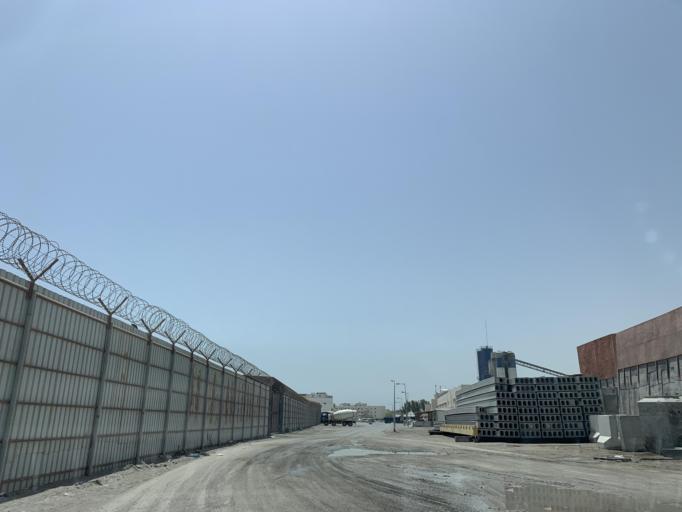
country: BH
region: Northern
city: Sitrah
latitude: 26.1488
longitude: 50.5977
